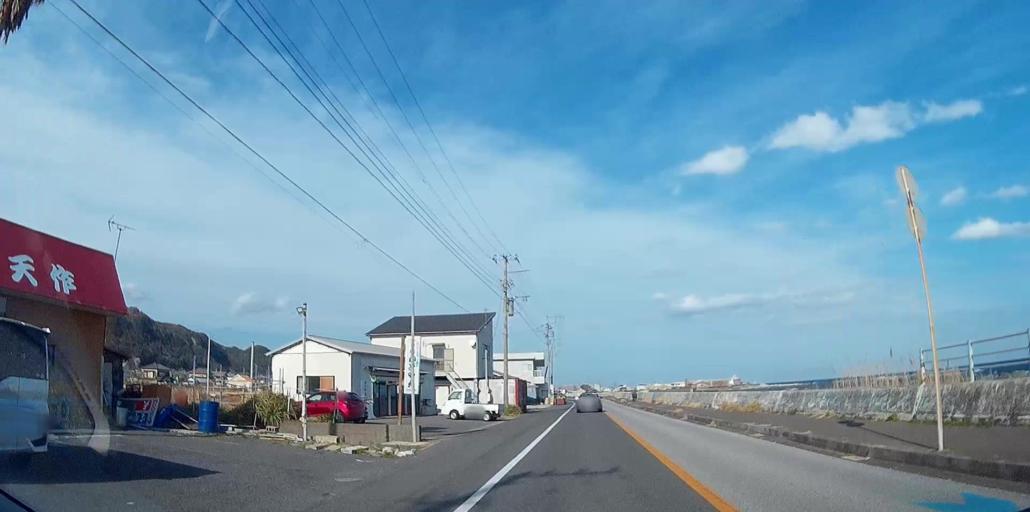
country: JP
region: Chiba
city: Tateyama
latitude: 34.9258
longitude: 139.9466
